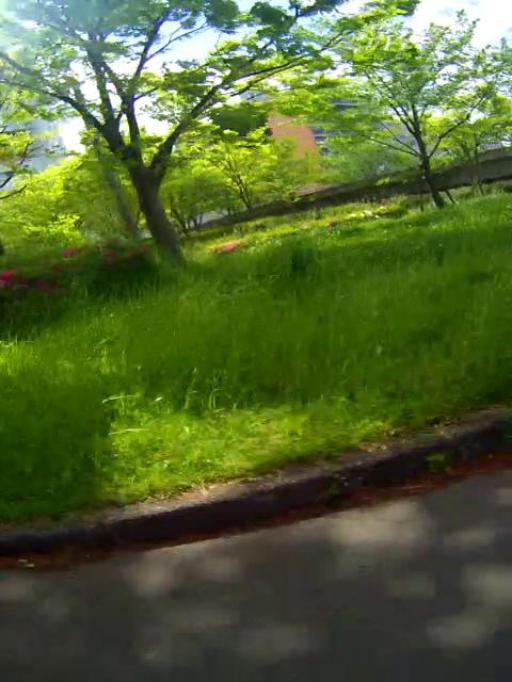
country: JP
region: Osaka
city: Osaka-shi
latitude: 34.7067
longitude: 135.5189
